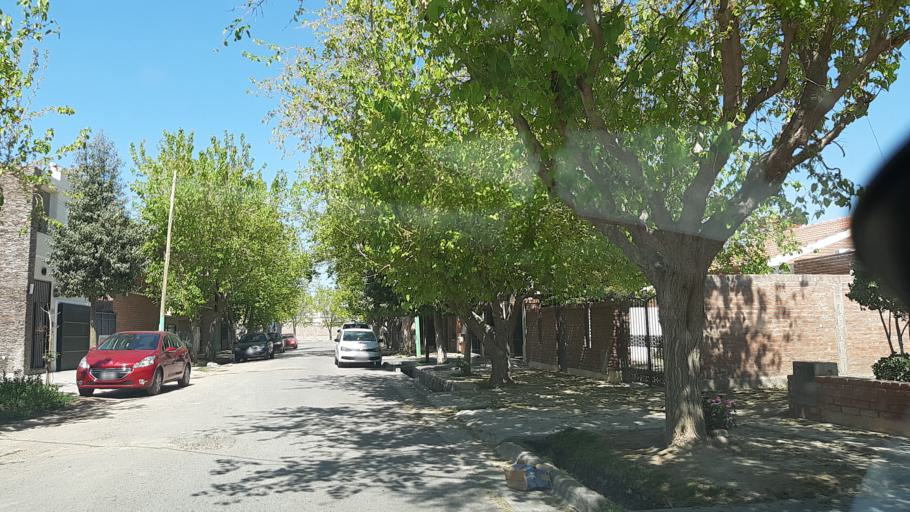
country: AR
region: San Juan
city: San Juan
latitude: -31.5222
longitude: -68.5887
